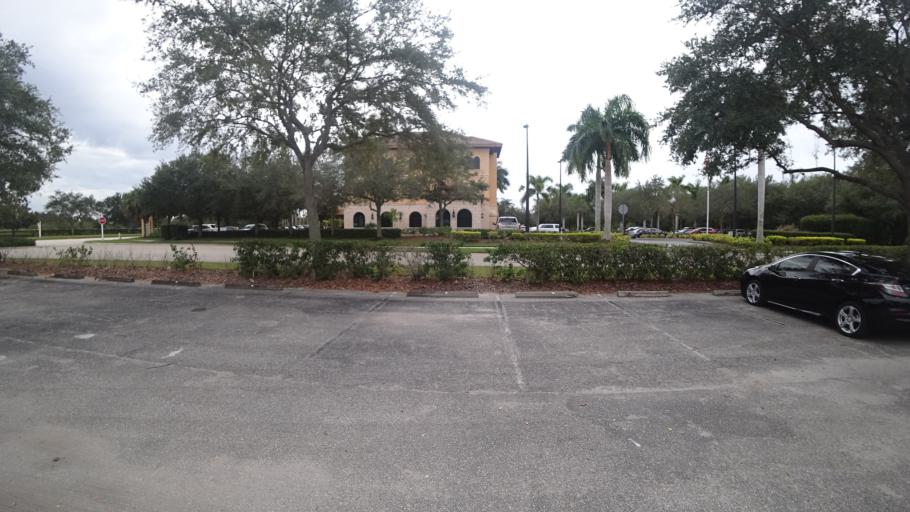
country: US
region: Florida
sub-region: Sarasota County
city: The Meadows
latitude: 27.3892
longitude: -82.4339
